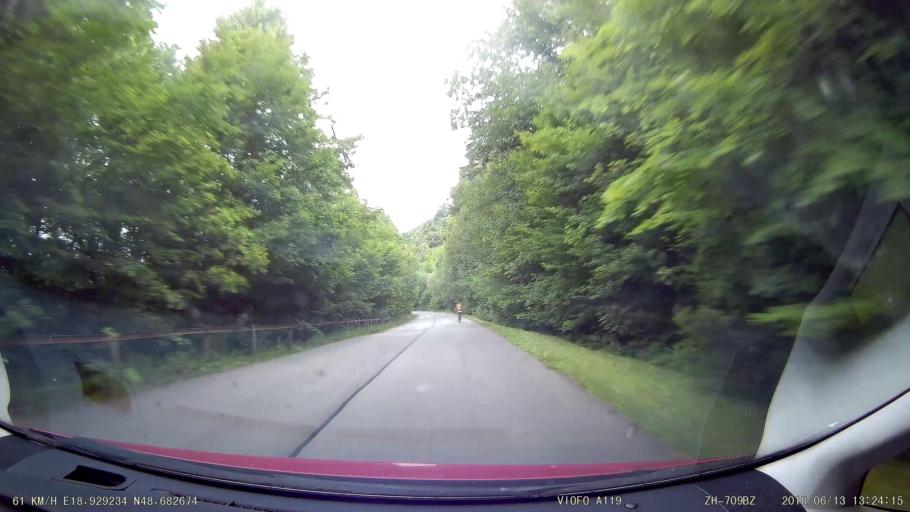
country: SK
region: Banskobystricky
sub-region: Okres Ziar nad Hronom
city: Kremnica
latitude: 48.6827
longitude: 18.9292
